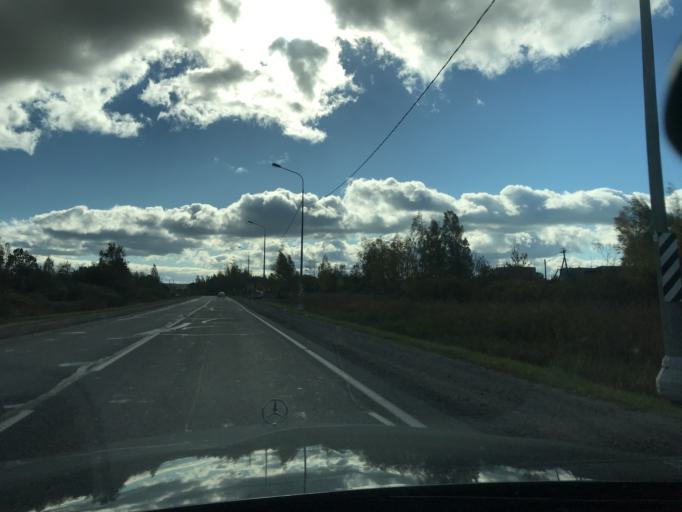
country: RU
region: Pskov
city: Ostrov
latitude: 57.3234
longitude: 28.3649
